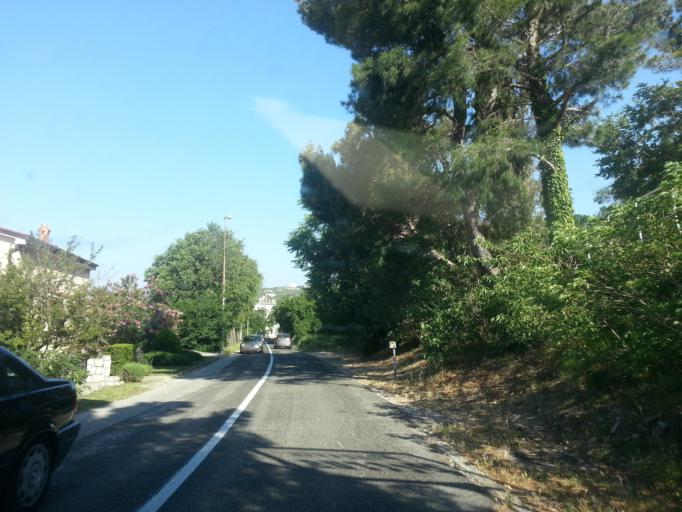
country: HR
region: Primorsko-Goranska
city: Kraljevica
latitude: 45.2771
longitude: 14.5701
